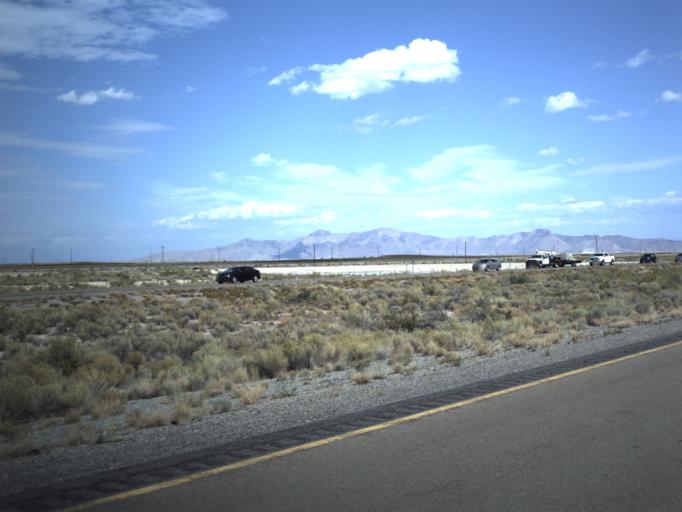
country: US
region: Utah
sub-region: Tooele County
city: Grantsville
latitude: 40.7541
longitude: -112.7377
